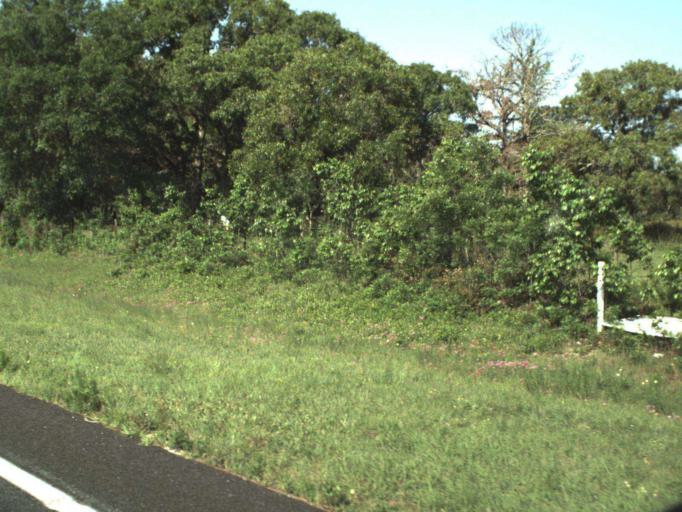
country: US
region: Florida
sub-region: Marion County
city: Citra
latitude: 29.3777
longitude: -82.1306
